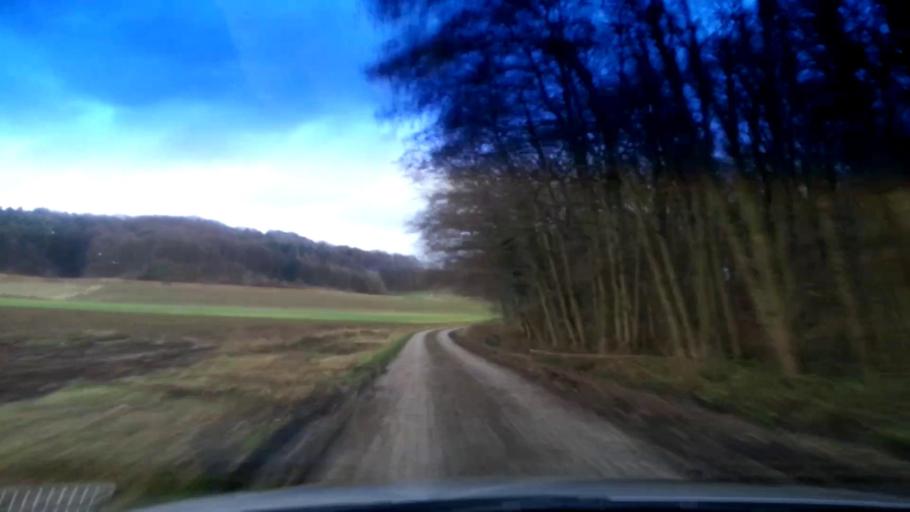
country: DE
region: Bavaria
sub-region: Upper Franconia
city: Schesslitz
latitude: 50.0093
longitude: 11.0289
